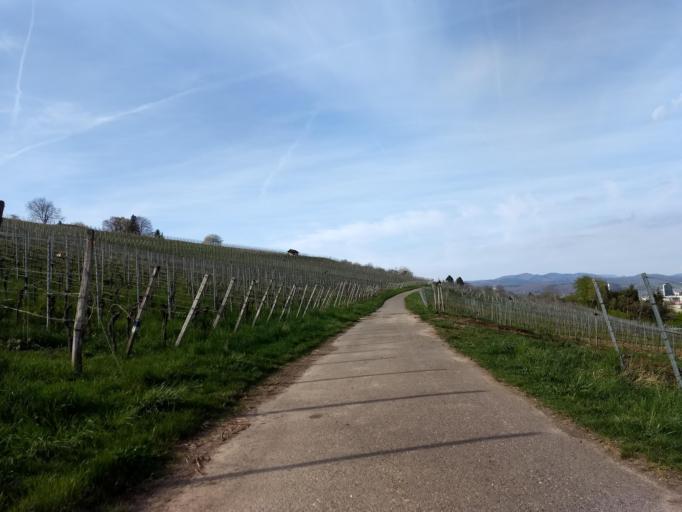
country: CH
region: Basel-City
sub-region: Basel-Stadt
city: Riehen
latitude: 47.5974
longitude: 7.6457
